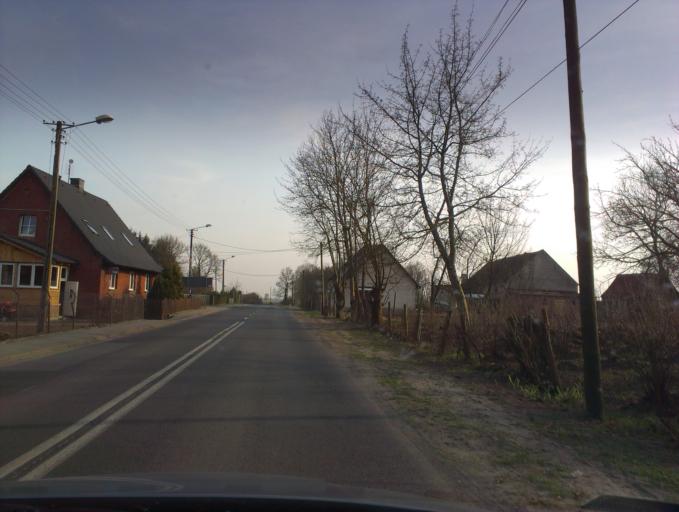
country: PL
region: Pomeranian Voivodeship
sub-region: Powiat czluchowski
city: Debrzno
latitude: 53.5245
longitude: 17.2312
